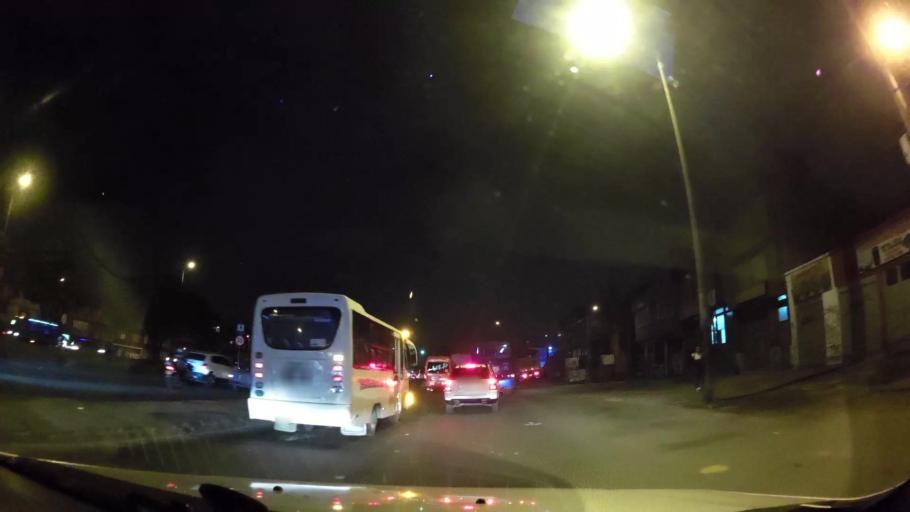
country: CO
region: Bogota D.C.
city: Bogota
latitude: 4.6057
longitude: -74.1421
